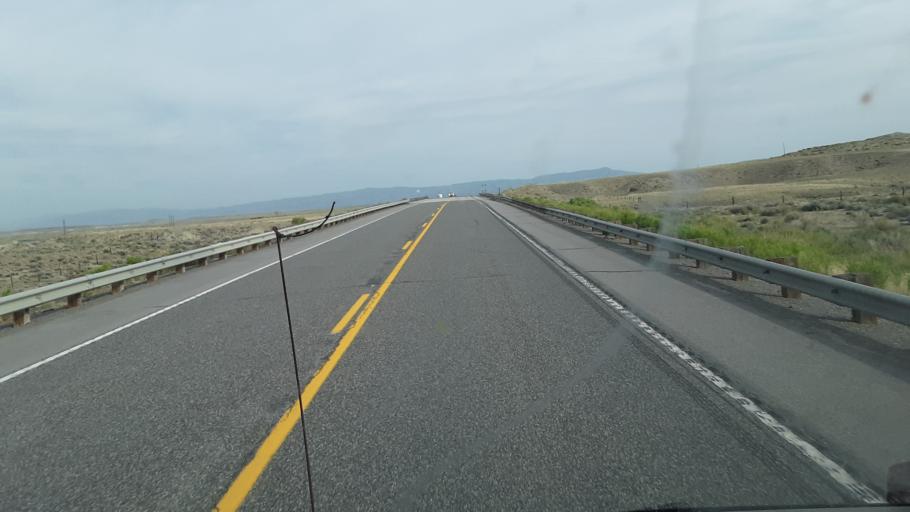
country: US
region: Wyoming
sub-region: Fremont County
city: Riverton
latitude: 43.2744
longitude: -108.1181
